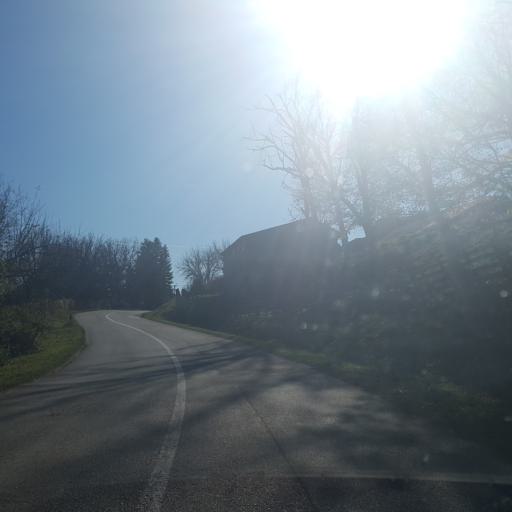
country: RS
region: Central Serbia
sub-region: Sumadijski Okrug
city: Raca
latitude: 44.2449
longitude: 20.8883
